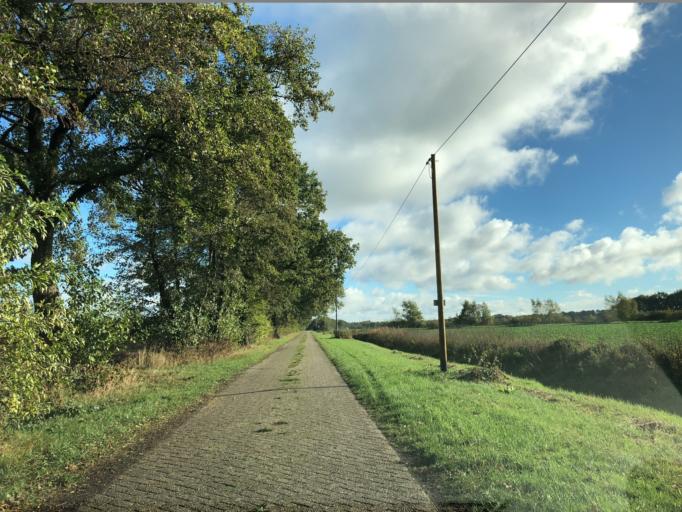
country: DE
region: Lower Saxony
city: Lehe
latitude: 53.0358
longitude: 7.3558
